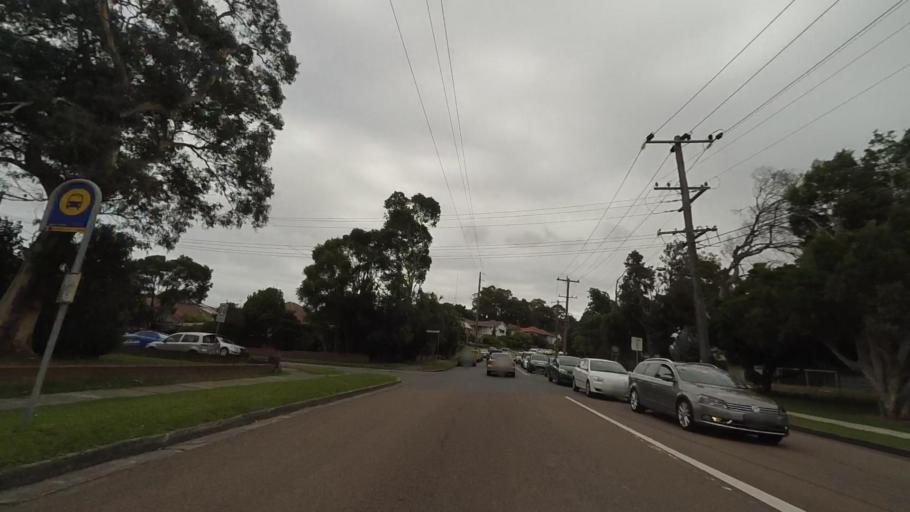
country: AU
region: New South Wales
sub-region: Lake Macquarie Shire
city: Highfields
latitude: -32.9420
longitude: 151.7052
